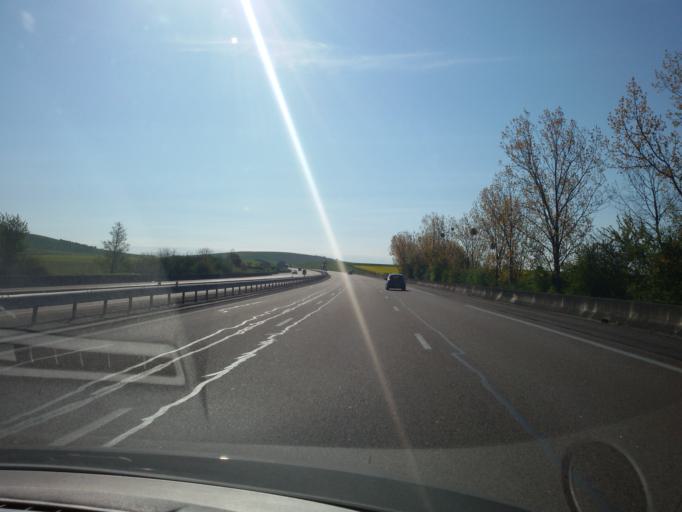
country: FR
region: Bourgogne
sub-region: Departement de l'Yonne
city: Aillant-sur-Tholon
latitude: 47.9009
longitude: 3.3532
